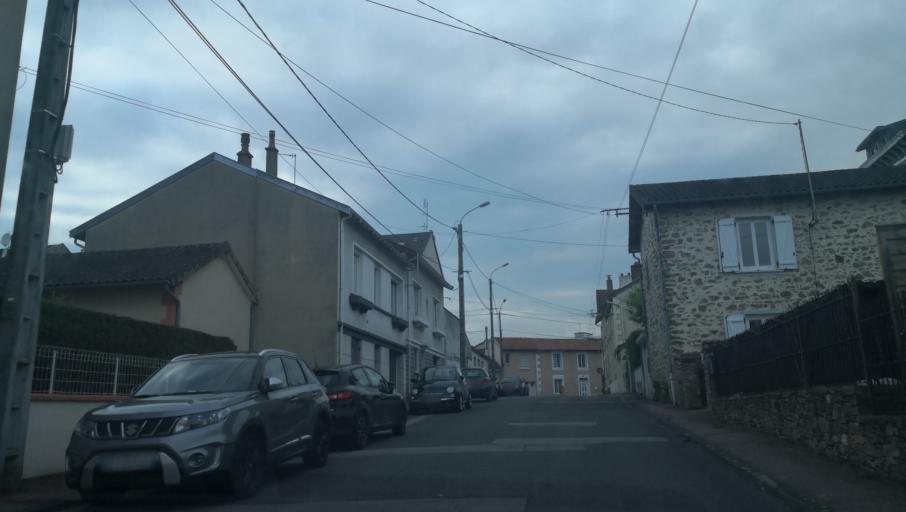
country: FR
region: Limousin
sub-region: Departement de la Haute-Vienne
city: Limoges
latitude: 45.8299
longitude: 1.2390
